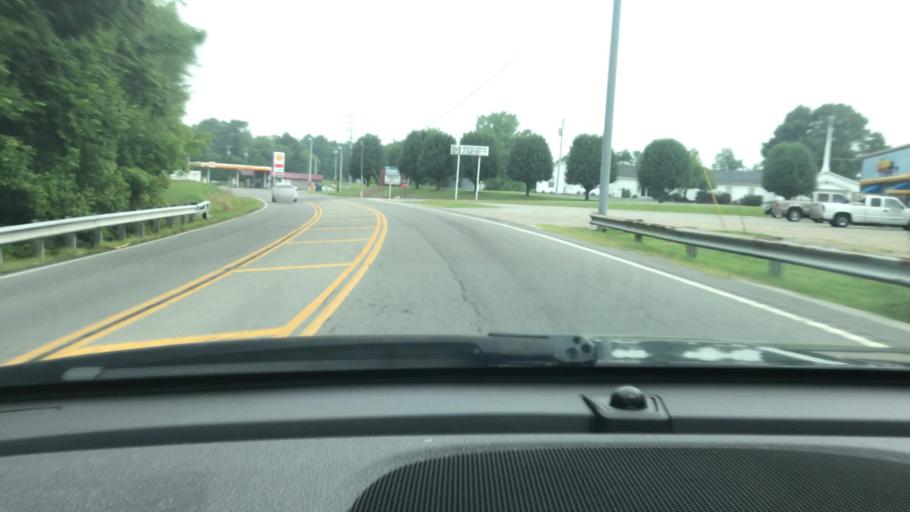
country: US
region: Tennessee
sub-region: Sumner County
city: Millersville
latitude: 36.4055
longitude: -86.6864
